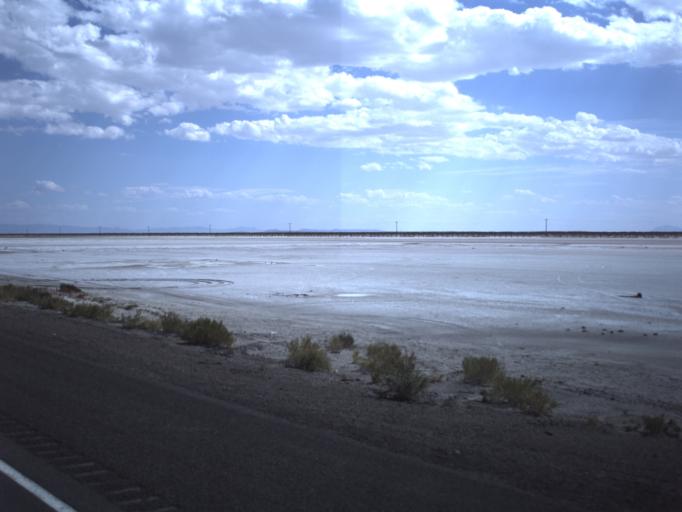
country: US
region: Utah
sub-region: Tooele County
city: Wendover
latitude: 40.7365
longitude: -113.7553
